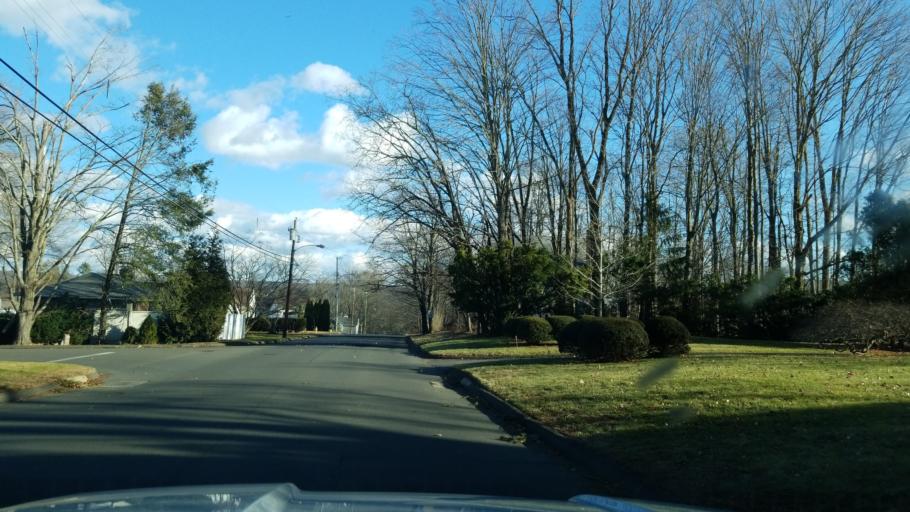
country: US
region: Connecticut
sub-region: Middlesex County
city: Middletown
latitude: 41.5404
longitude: -72.6593
